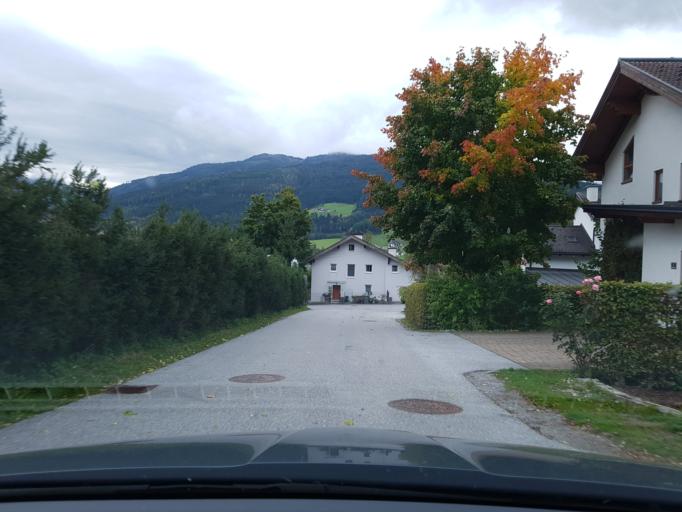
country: AT
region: Salzburg
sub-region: Politischer Bezirk Sankt Johann im Pongau
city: Radstadt
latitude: 47.3868
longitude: 13.4706
